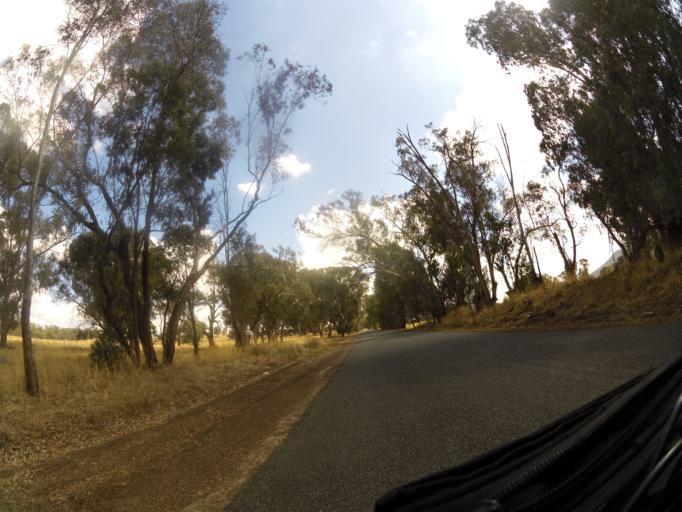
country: AU
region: Victoria
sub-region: Benalla
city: Benalla
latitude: -36.7329
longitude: 146.0968
